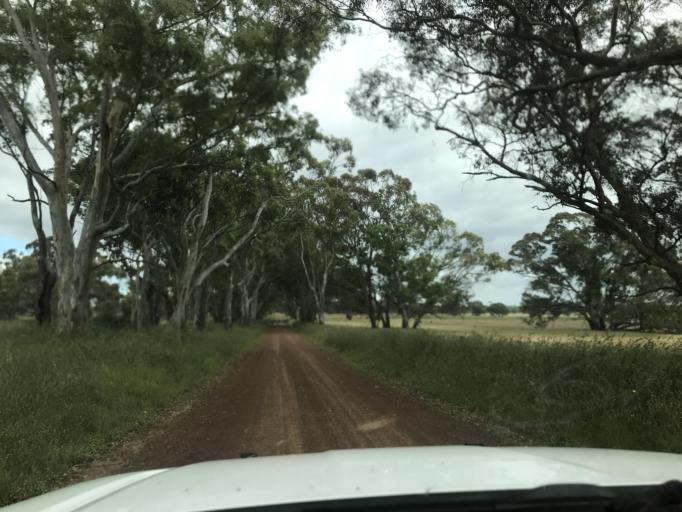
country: AU
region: South Australia
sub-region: Wattle Range
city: Penola
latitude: -37.1027
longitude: 141.2396
